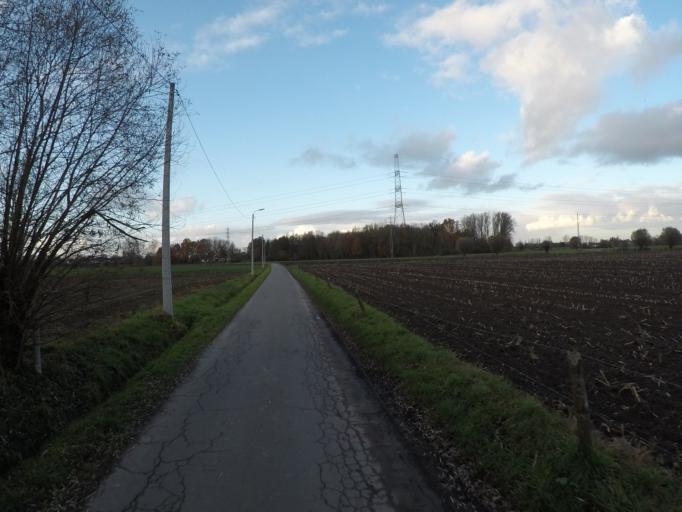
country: BE
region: Flanders
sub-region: Provincie Vlaams-Brabant
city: Londerzeel
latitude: 51.0202
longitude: 4.3072
